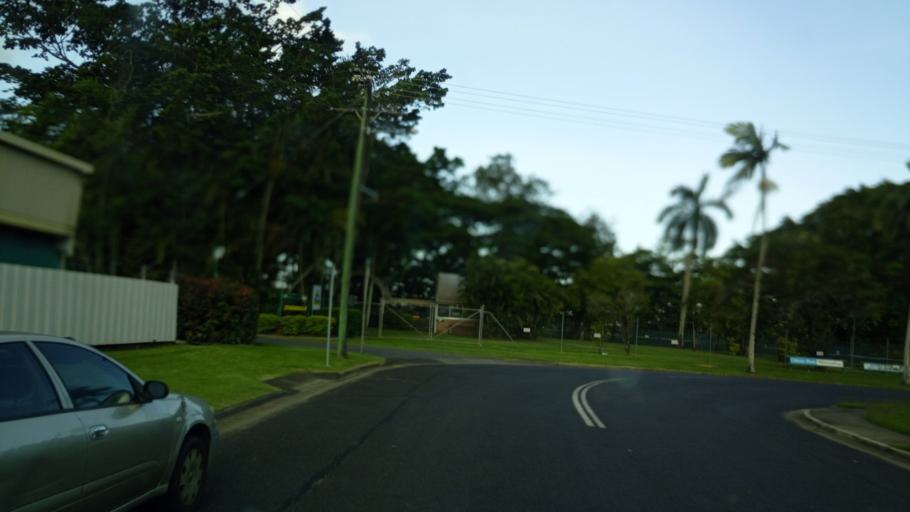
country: AU
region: Queensland
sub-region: Cairns
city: Woree
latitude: -16.9387
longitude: 145.7432
